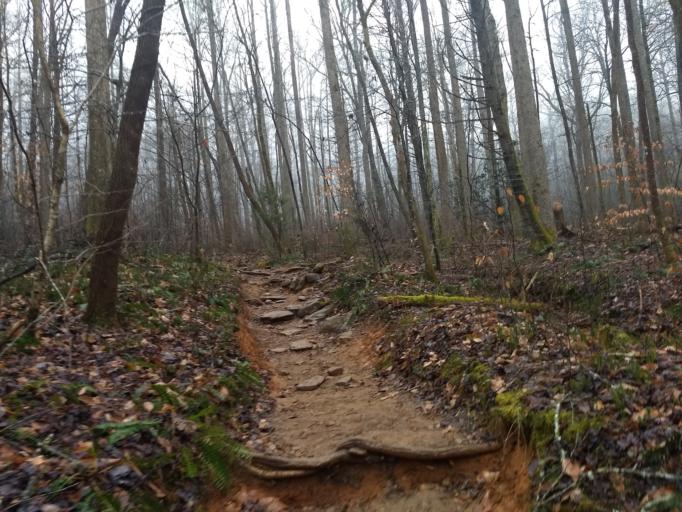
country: US
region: North Carolina
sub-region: Transylvania County
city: Brevard
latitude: 35.2748
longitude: -82.7823
